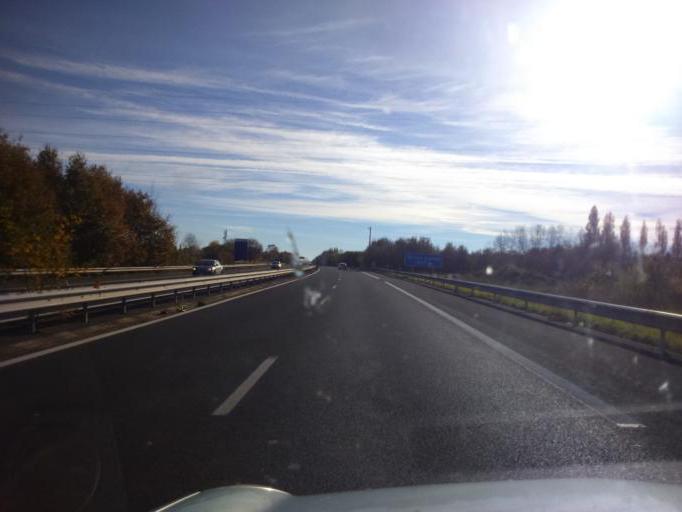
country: FR
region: Poitou-Charentes
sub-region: Departement de la Charente-Maritime
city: Breuil-Magne
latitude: 45.9672
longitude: -0.9797
